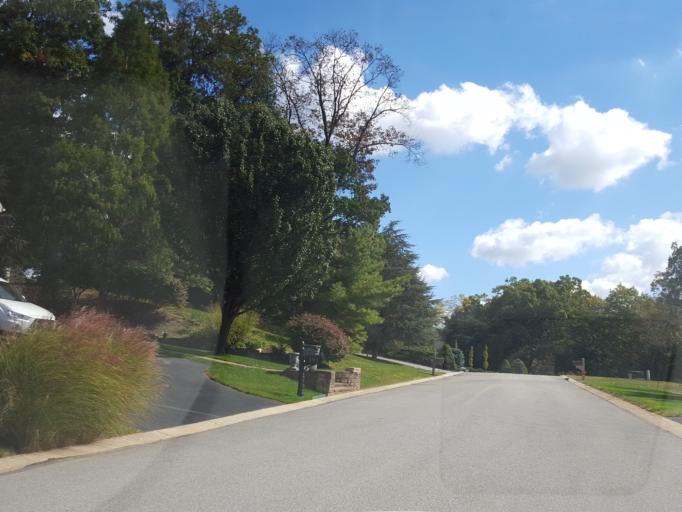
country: US
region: Pennsylvania
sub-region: York County
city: East York
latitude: 39.9495
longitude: -76.6700
